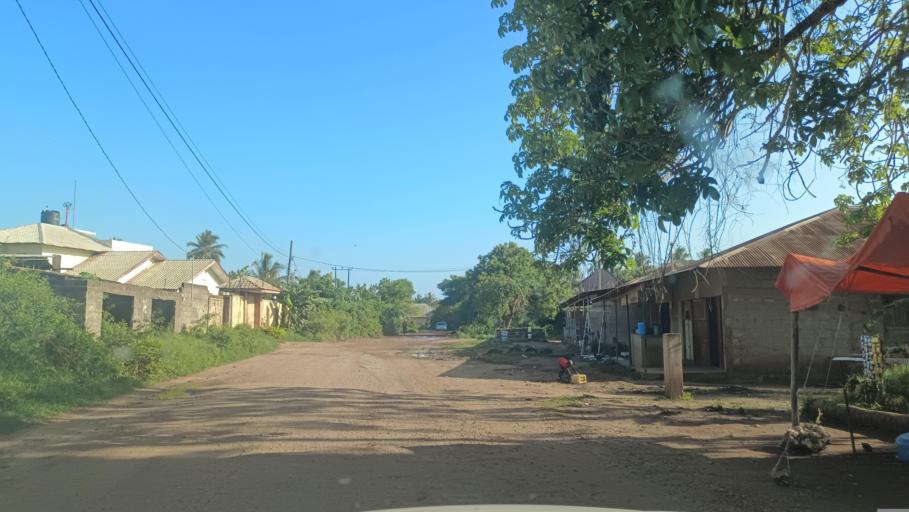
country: TZ
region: Zanzibar Urban/West
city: Zanzibar
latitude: -6.2390
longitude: 39.2204
